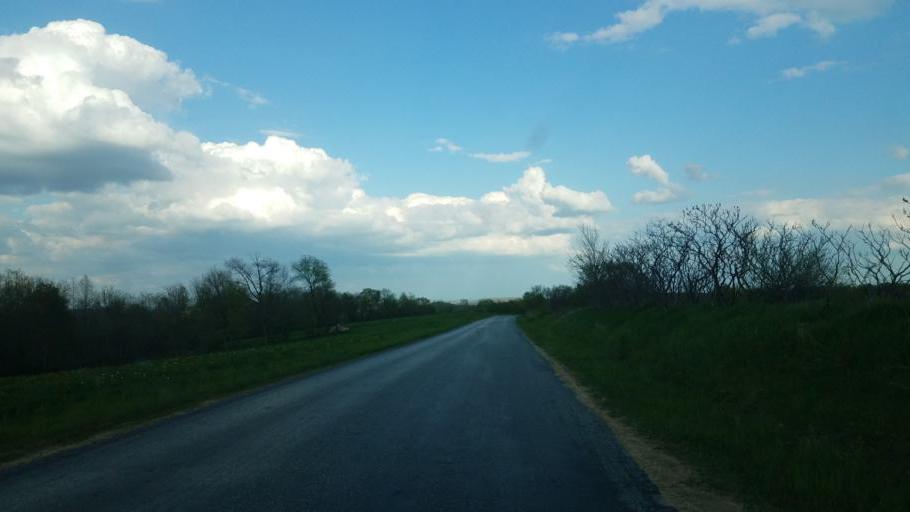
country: US
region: Wisconsin
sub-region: Vernon County
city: Hillsboro
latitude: 43.6841
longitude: -90.3782
